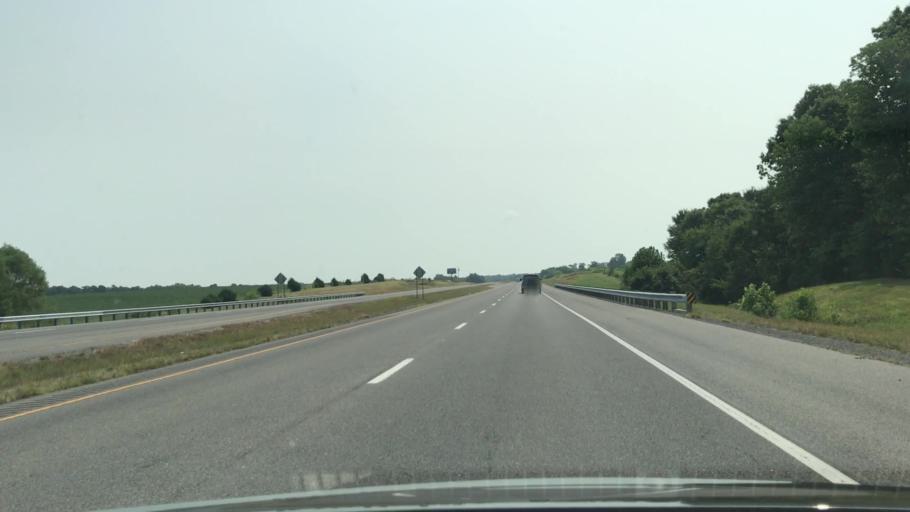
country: US
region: Kentucky
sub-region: Calloway County
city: Murray
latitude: 36.6501
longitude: -88.2617
